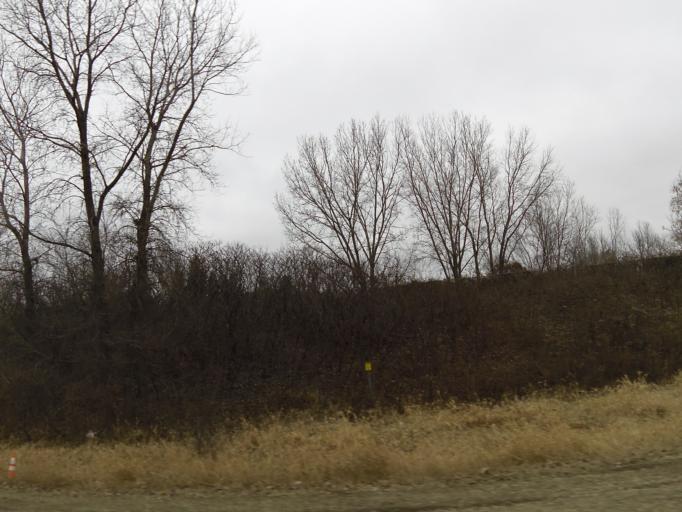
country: US
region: Minnesota
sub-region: Dakota County
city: Eagan
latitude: 44.8151
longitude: -93.1750
